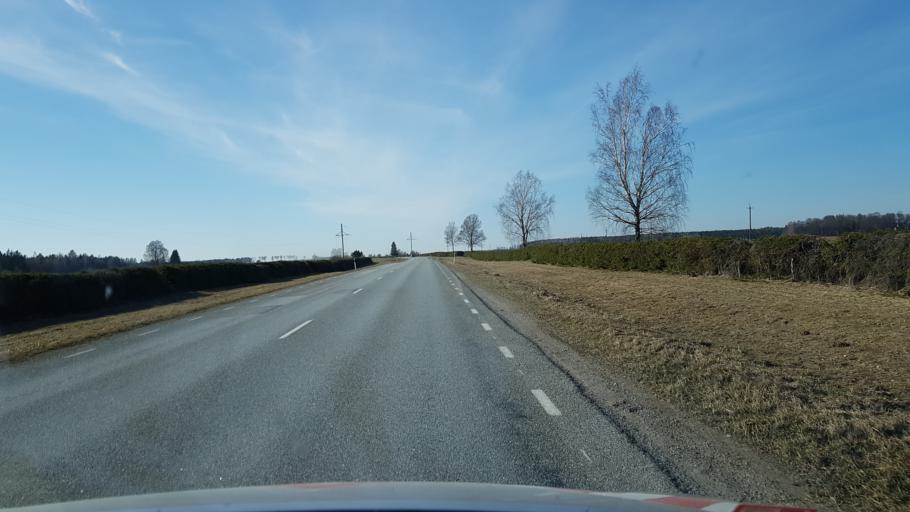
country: EE
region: Laeaene-Virumaa
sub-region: Vinni vald
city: Vinni
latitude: 59.2101
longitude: 26.5506
